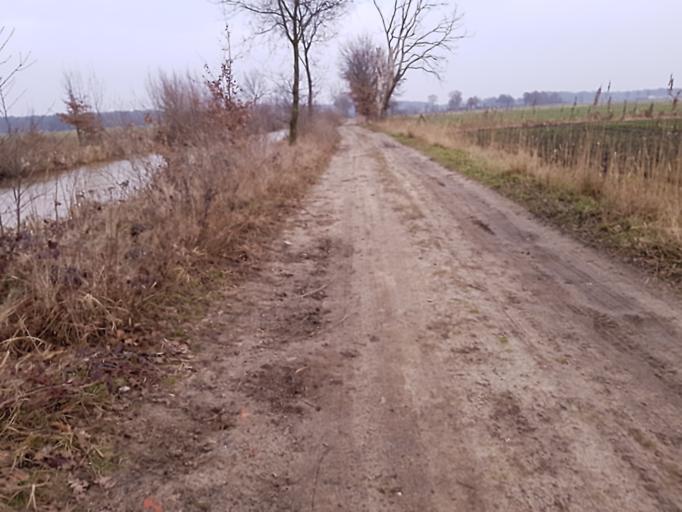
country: BE
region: Flanders
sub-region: Provincie Antwerpen
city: Stabroek
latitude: 51.3419
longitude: 4.3708
